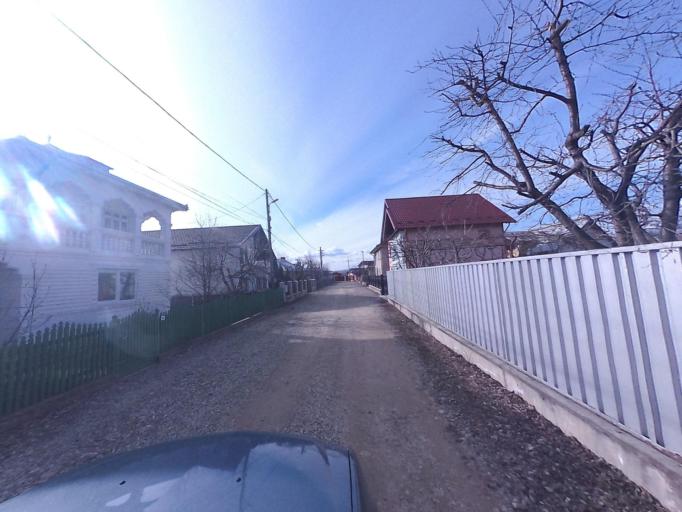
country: RO
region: Neamt
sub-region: Oras Targu Neamt
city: Humulesti
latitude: 47.2086
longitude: 26.3473
